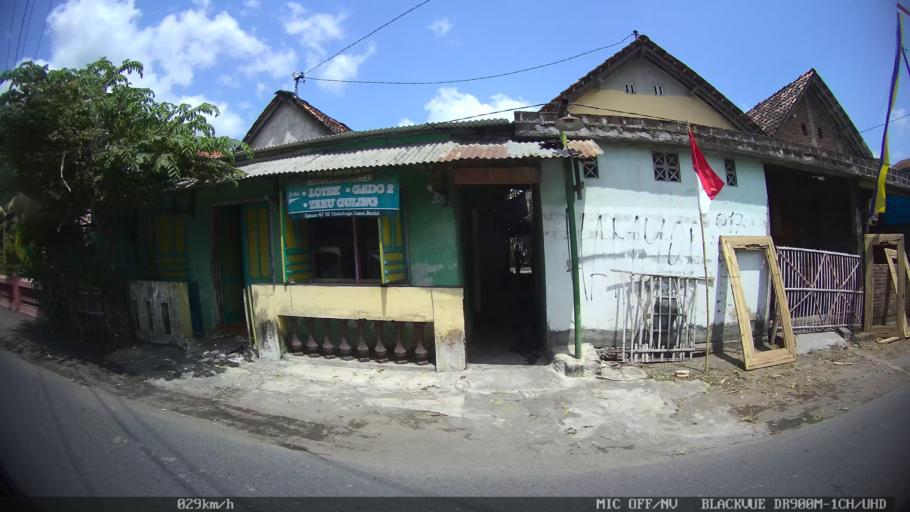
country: ID
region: Daerah Istimewa Yogyakarta
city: Sewon
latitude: -7.8733
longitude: 110.3690
